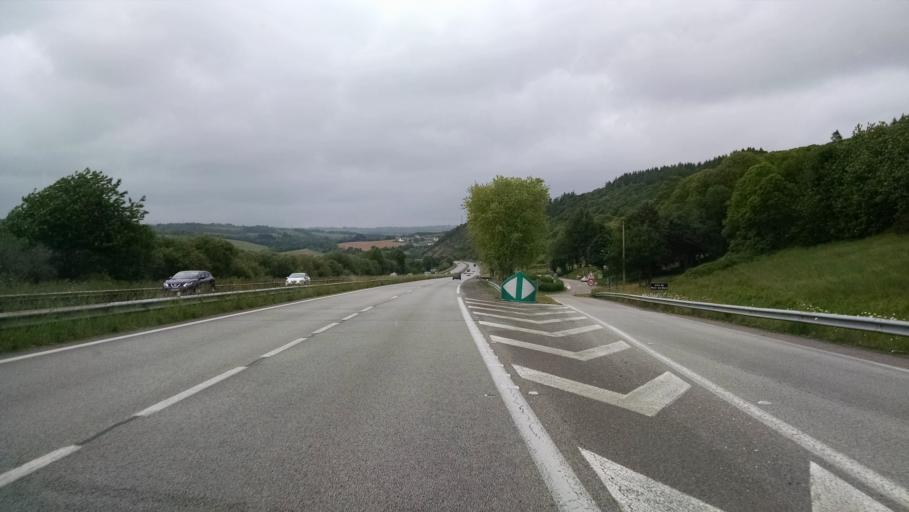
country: FR
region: Brittany
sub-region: Departement du Finistere
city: Chateaulin
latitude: 48.2372
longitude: -4.1052
